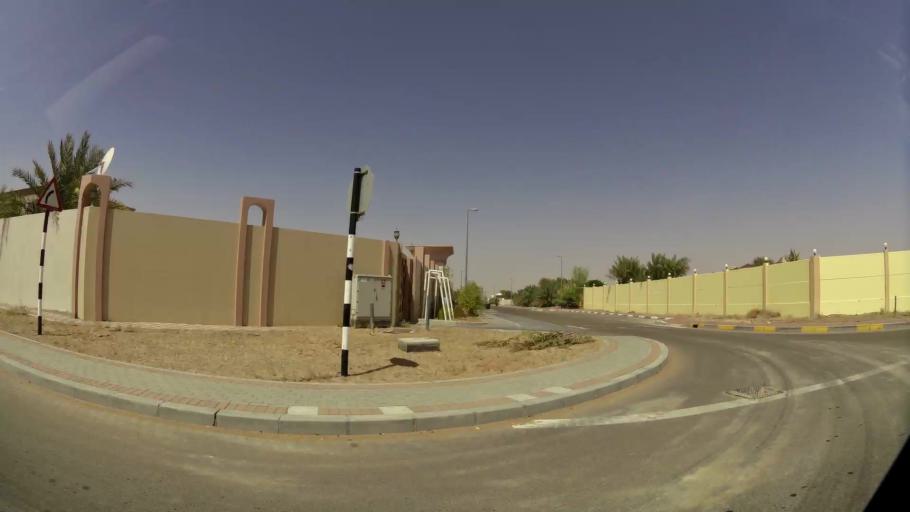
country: OM
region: Al Buraimi
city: Al Buraymi
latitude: 24.2973
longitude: 55.7618
